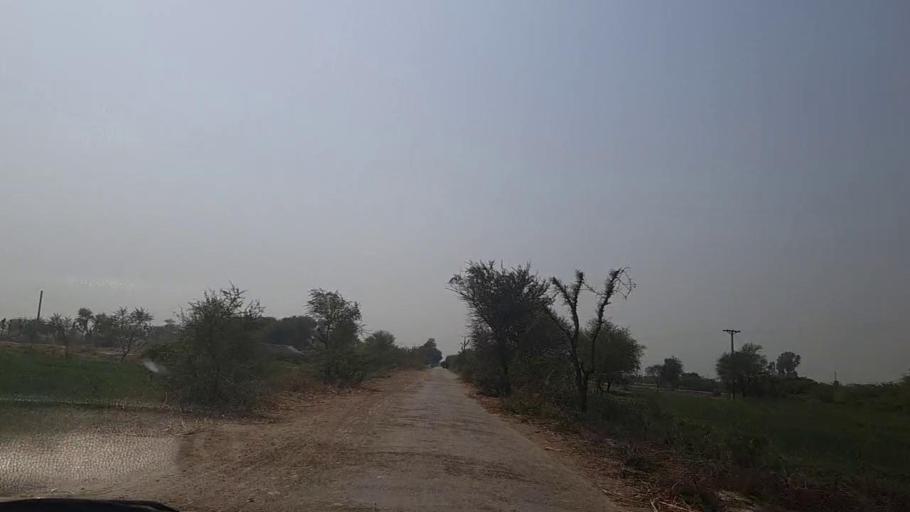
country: PK
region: Sindh
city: Pithoro
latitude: 25.5633
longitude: 69.2570
